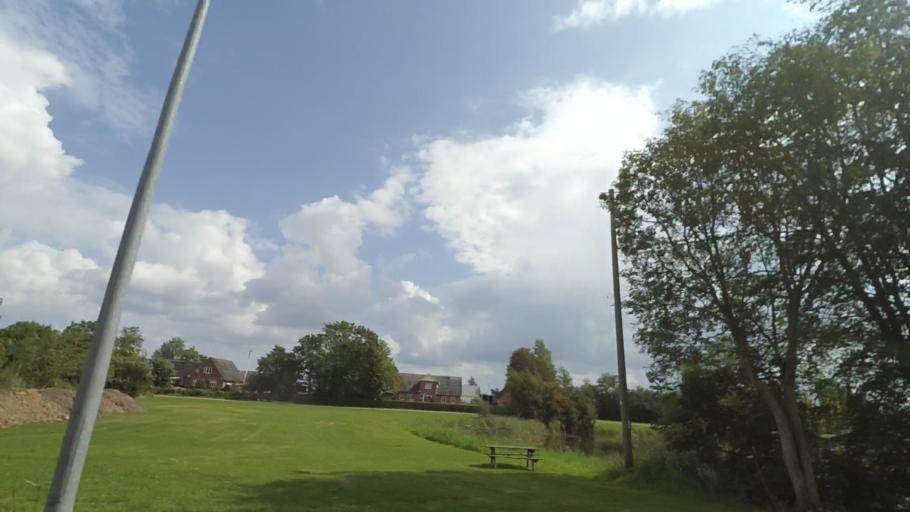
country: DK
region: Central Jutland
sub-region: Norddjurs Kommune
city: Allingabro
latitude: 56.5398
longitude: 10.3625
